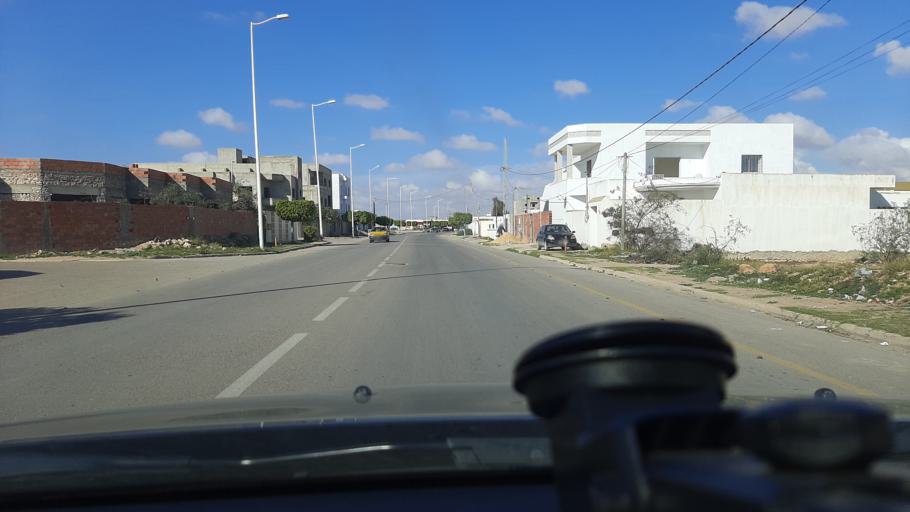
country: TN
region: Safaqis
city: Sfax
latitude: 34.8090
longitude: 10.7117
